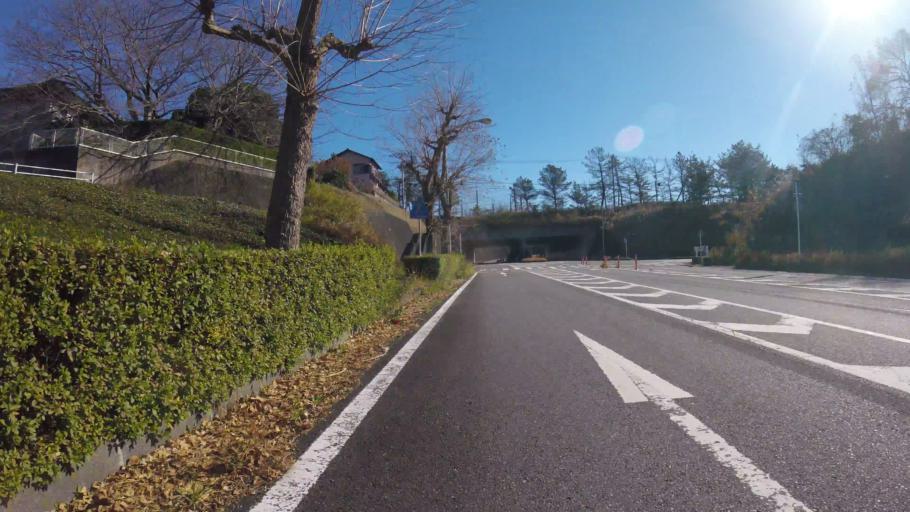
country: JP
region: Shizuoka
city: Mishima
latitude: 35.1285
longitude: 138.9399
